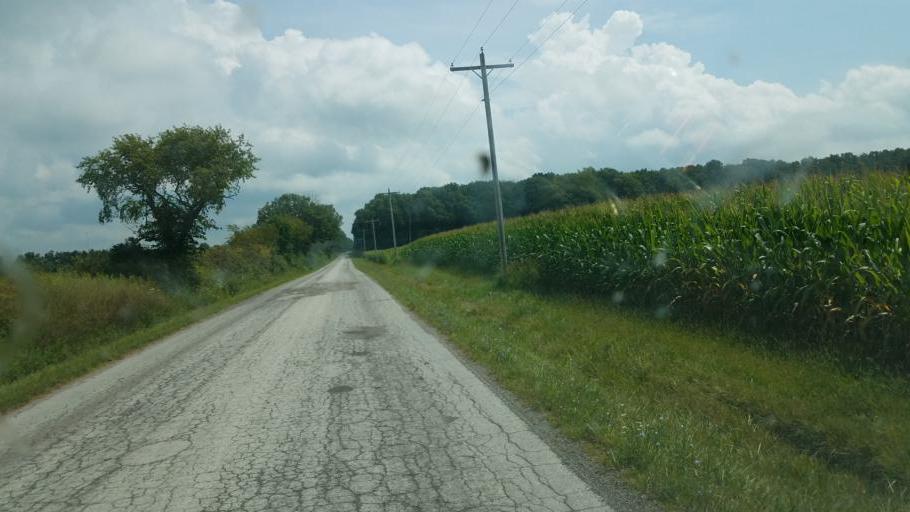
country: US
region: Ohio
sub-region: Morrow County
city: Mount Gilead
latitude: 40.6019
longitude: -82.7176
